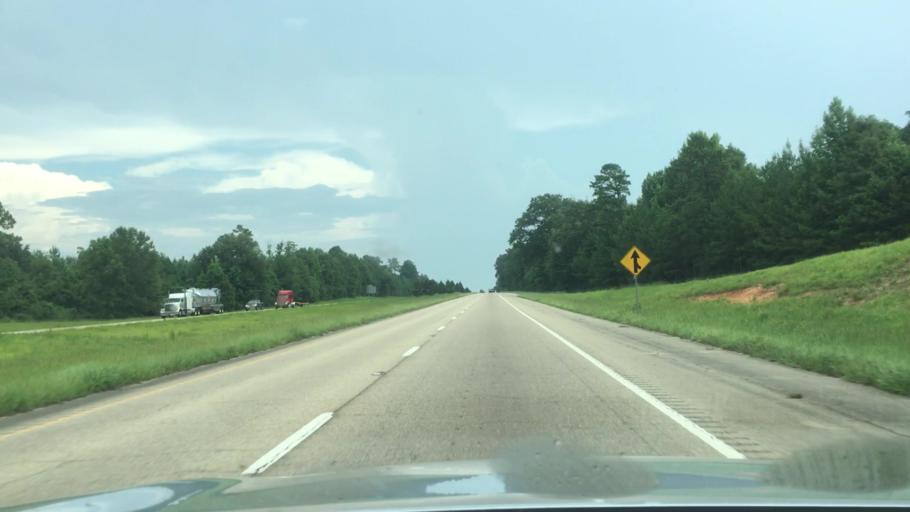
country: US
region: Mississippi
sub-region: Lamar County
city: Lumberton
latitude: 31.0016
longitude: -89.4181
